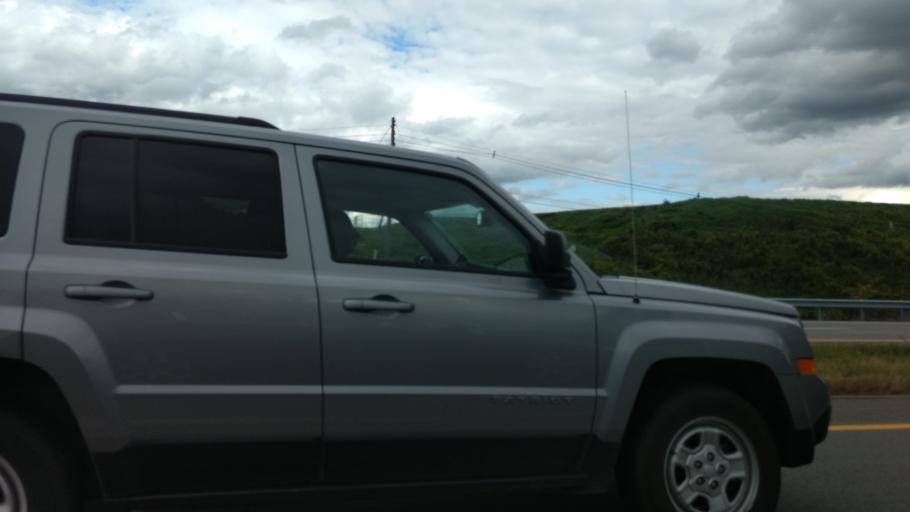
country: US
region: Pennsylvania
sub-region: Westmoreland County
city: Fellsburg
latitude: 40.2076
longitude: -79.8402
